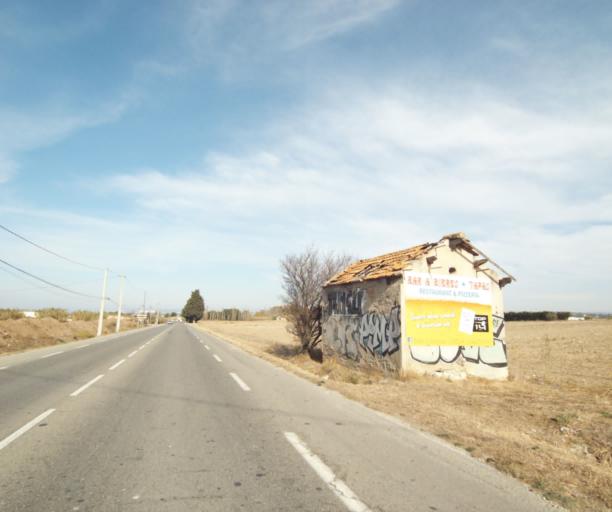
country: FR
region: Provence-Alpes-Cote d'Azur
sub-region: Departement des Bouches-du-Rhone
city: Chateauneuf-les-Martigues
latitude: 43.3884
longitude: 5.1934
